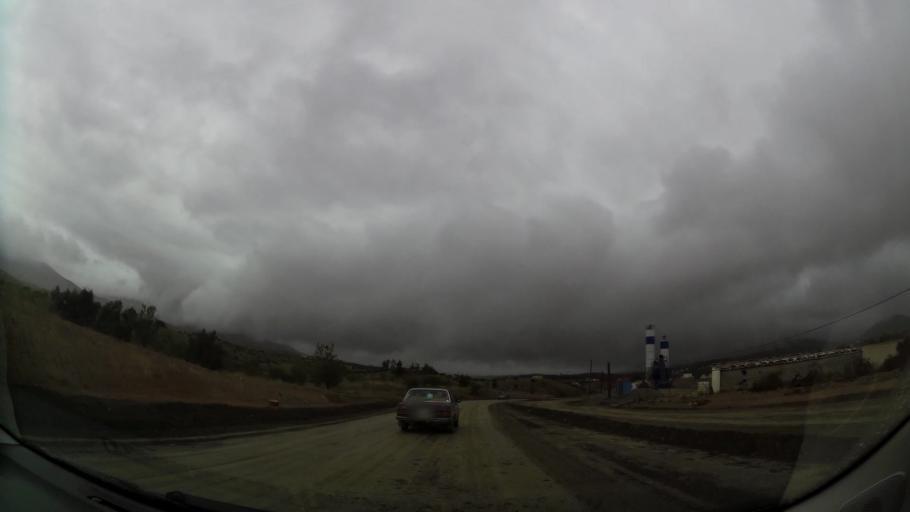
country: MA
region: Oriental
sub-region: Nador
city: Midar
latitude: 34.8957
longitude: -3.7700
